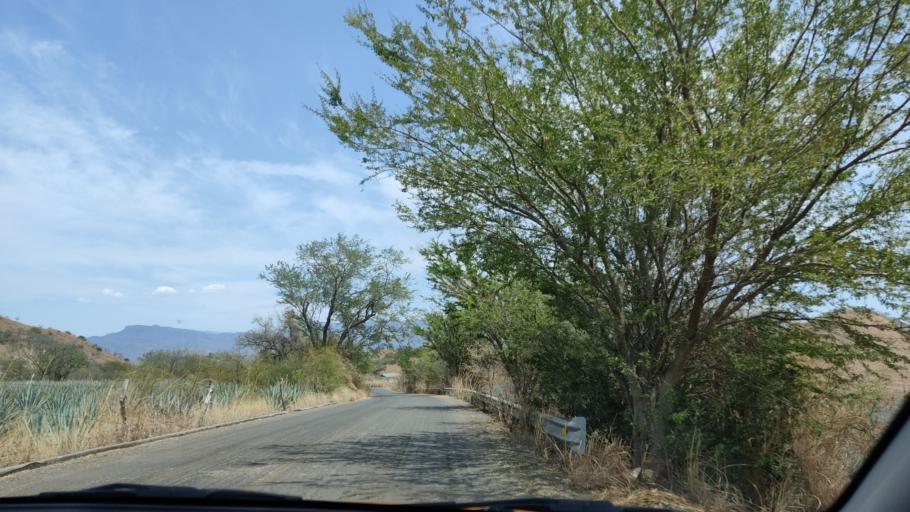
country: MX
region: Nayarit
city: Santa Maria del Oro
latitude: 21.5001
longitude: -104.6185
